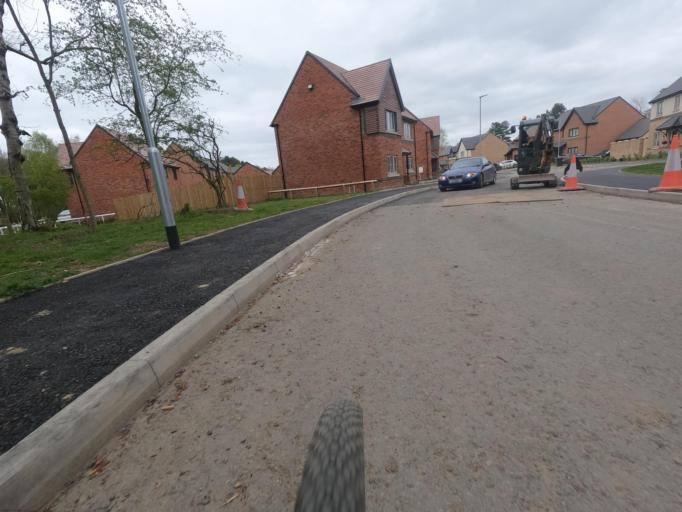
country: GB
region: England
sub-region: Northumberland
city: Ponteland
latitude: 55.0601
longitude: -1.7640
